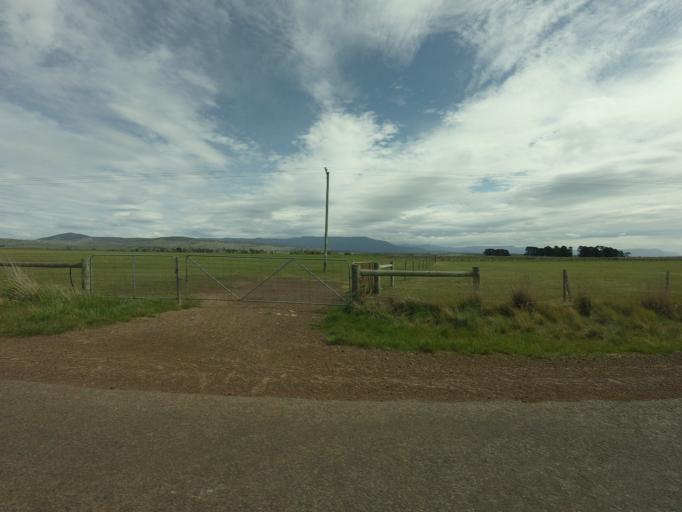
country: AU
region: Tasmania
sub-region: Northern Midlands
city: Evandale
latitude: -41.8583
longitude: 147.3444
